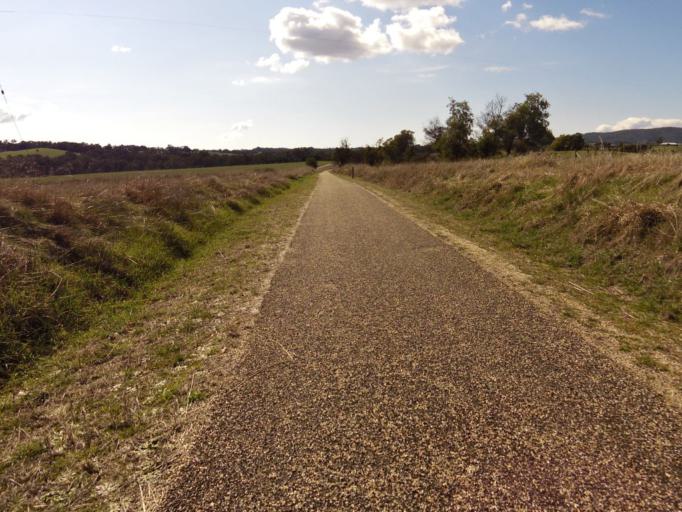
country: AU
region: Victoria
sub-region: Wangaratta
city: Wangaratta
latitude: -36.3974
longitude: 146.6519
